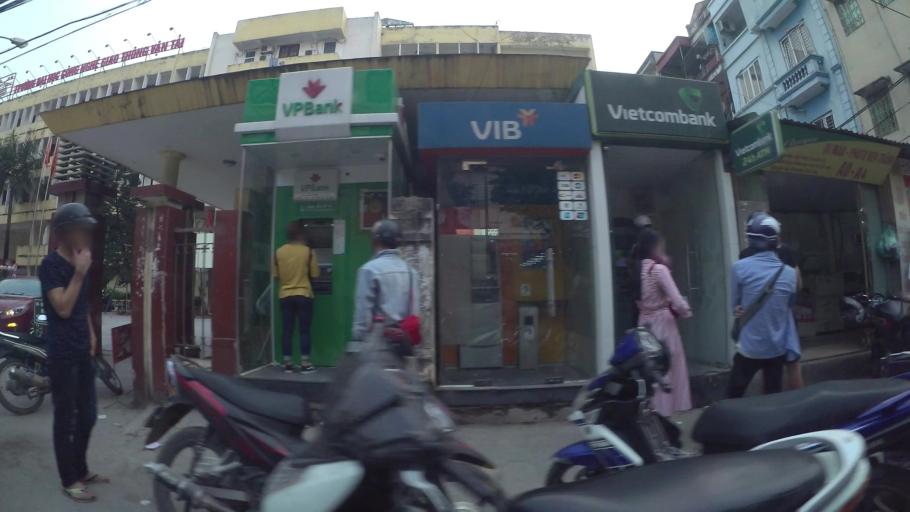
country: VN
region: Ha Noi
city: Thanh Xuan
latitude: 20.9852
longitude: 105.7990
